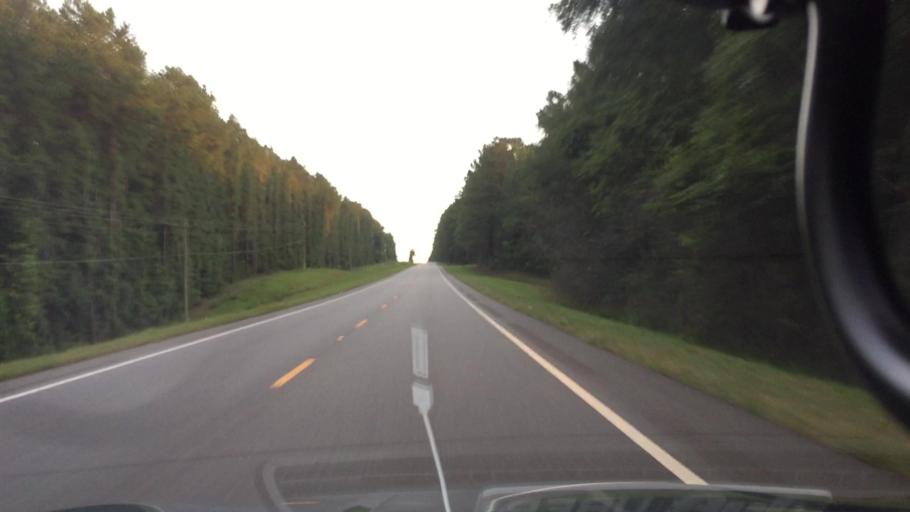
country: US
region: Alabama
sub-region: Coffee County
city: New Brockton
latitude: 31.5240
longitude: -85.9175
